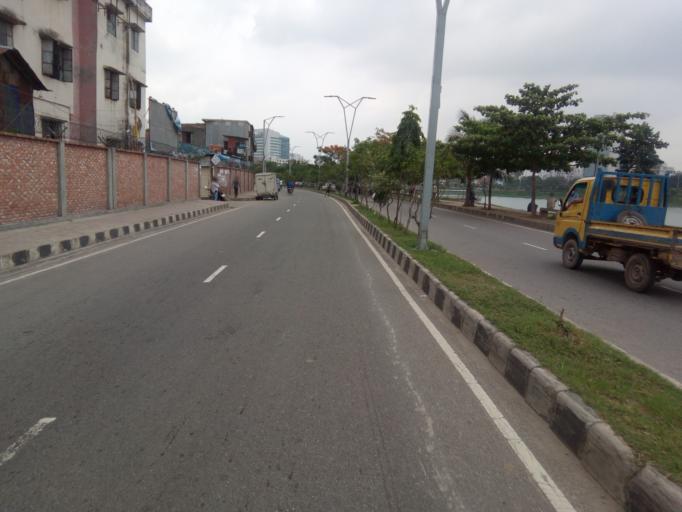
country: BD
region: Dhaka
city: Paltan
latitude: 23.7658
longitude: 90.4109
